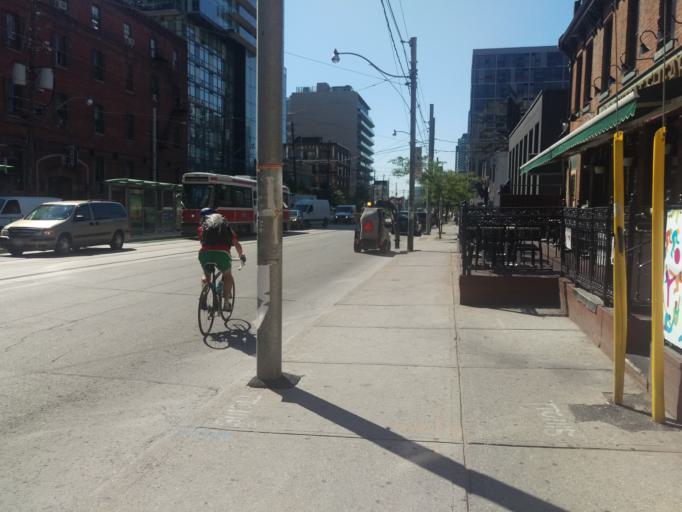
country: CA
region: Ontario
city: Toronto
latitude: 43.6437
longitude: -79.4027
